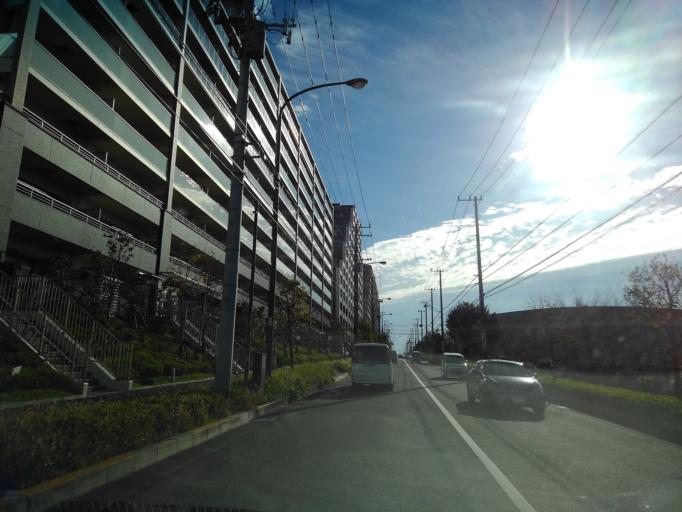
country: JP
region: Tokyo
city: Hachioji
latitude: 35.6065
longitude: 139.3529
